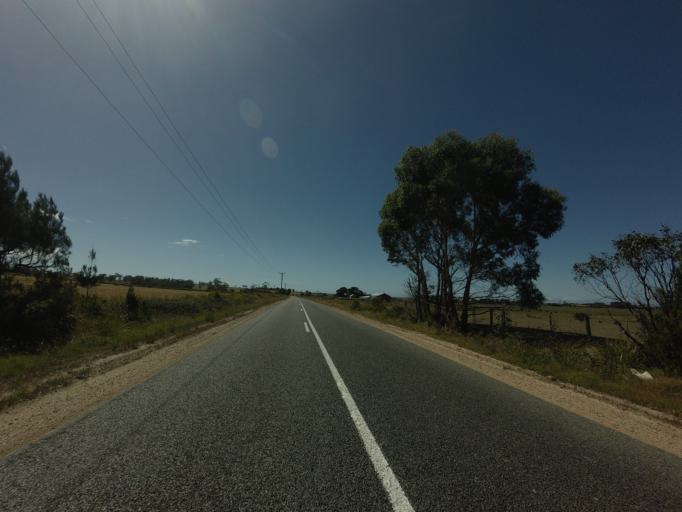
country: AU
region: Tasmania
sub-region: Break O'Day
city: St Helens
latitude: -41.7776
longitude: 148.2586
